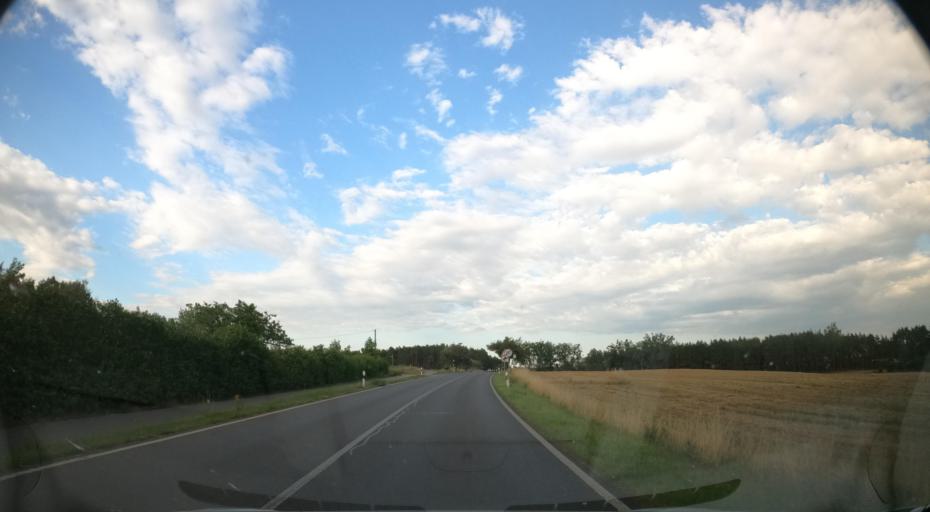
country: PL
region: West Pomeranian Voivodeship
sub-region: Powiat policki
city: Dobra
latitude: 53.4564
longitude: 14.2916
